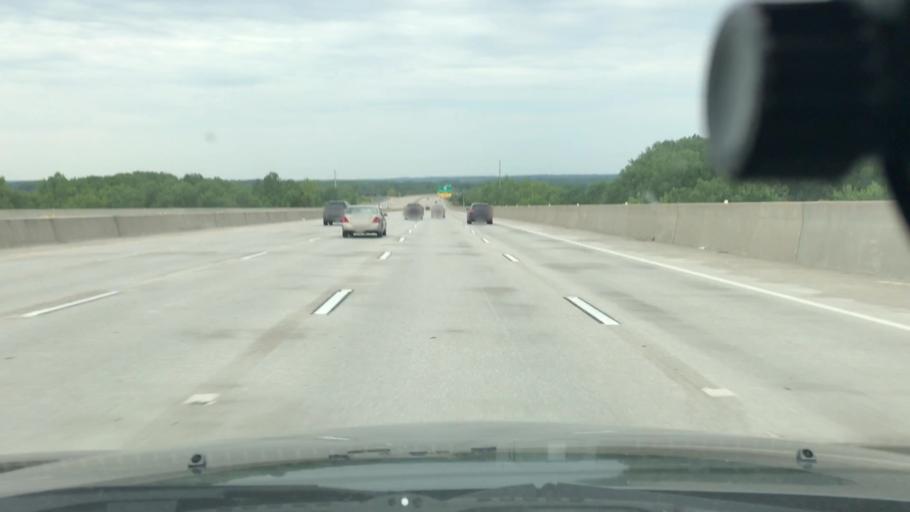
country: US
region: Missouri
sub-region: Saint Louis County
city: Maryland Heights
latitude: 38.7065
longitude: -90.4874
